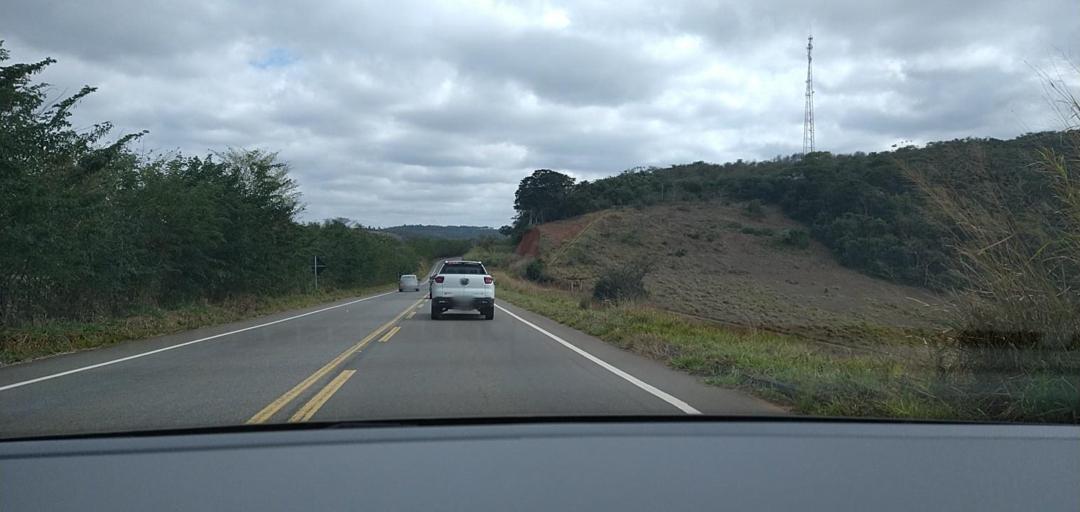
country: BR
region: Minas Gerais
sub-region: Ponte Nova
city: Ponte Nova
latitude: -20.5371
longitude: -42.8896
